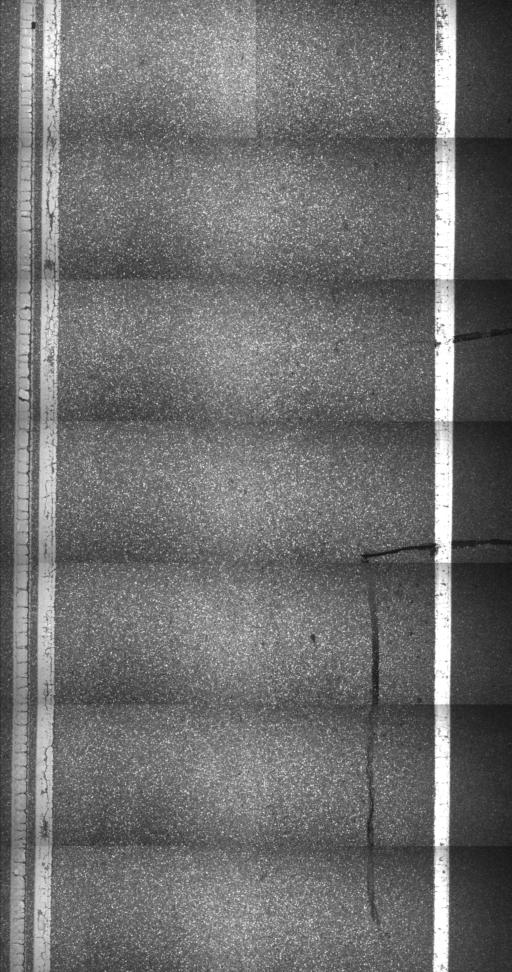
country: US
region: Vermont
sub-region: Windsor County
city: Wilder
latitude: 43.7032
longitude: -72.4087
